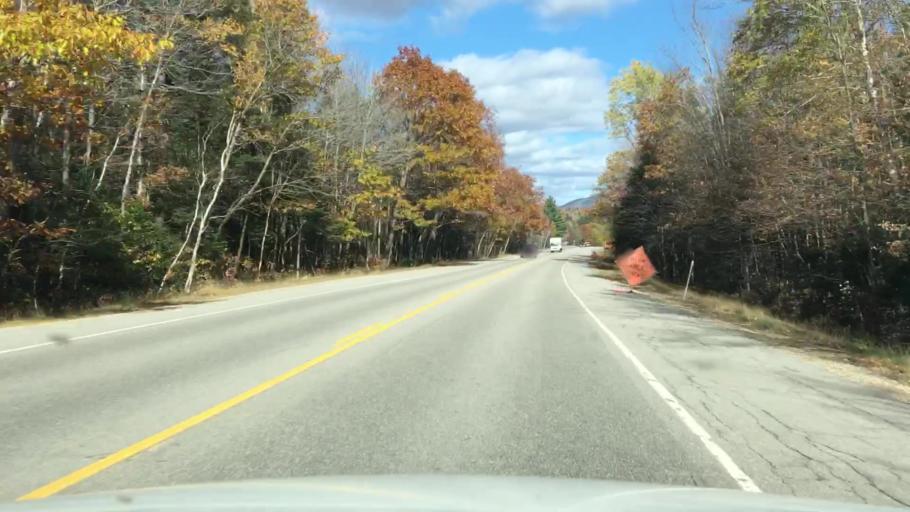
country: US
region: New Hampshire
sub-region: Coos County
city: Gorham
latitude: 44.3324
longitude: -71.2118
